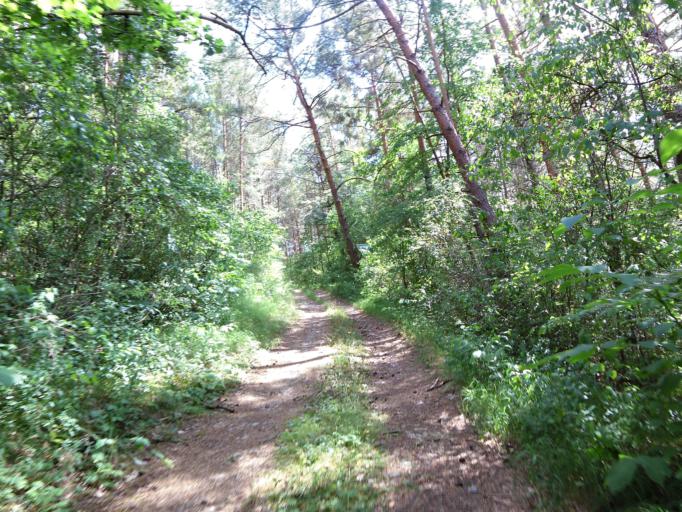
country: DE
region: Bavaria
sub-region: Regierungsbezirk Unterfranken
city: Gerbrunn
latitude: 49.7720
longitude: 9.9977
